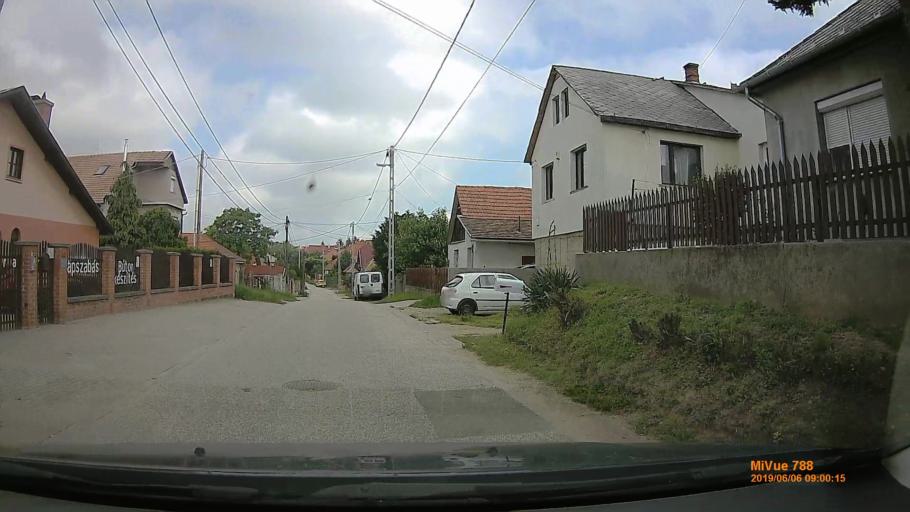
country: HU
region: Pest
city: Maglod
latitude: 47.4488
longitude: 19.3450
